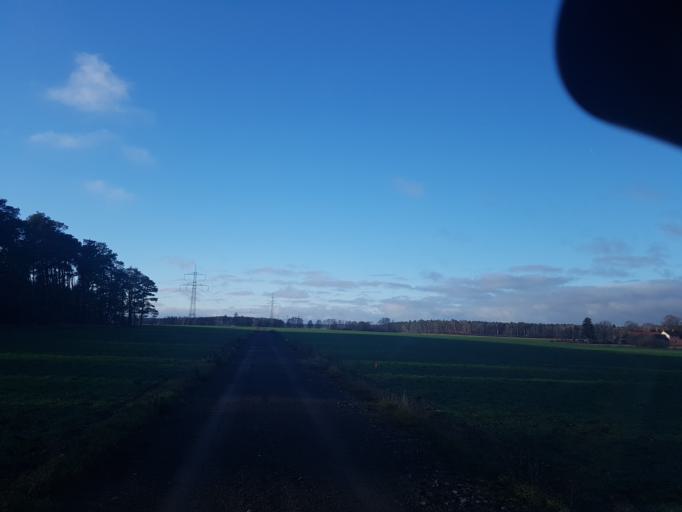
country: DE
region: Brandenburg
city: Schonborn
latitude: 51.5585
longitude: 13.4801
